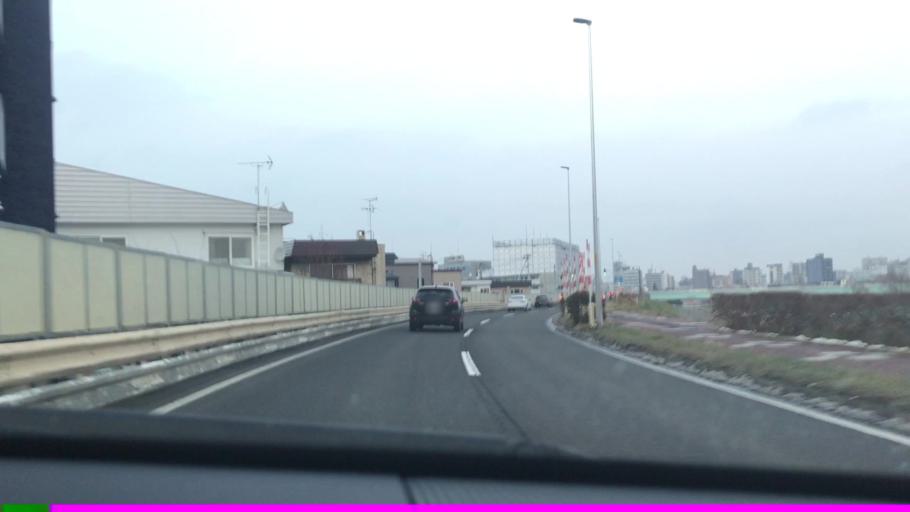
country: JP
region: Hokkaido
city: Sapporo
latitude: 43.0272
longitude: 141.3514
